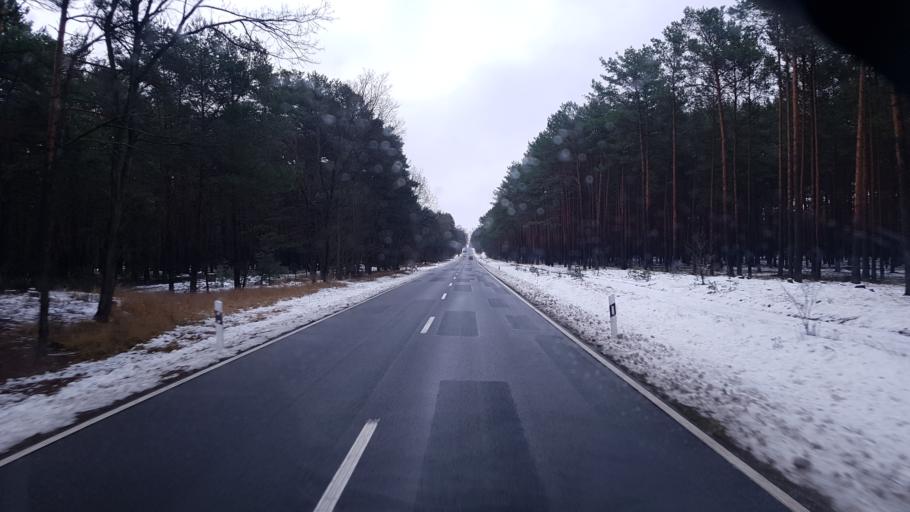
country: DE
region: Brandenburg
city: Jamlitz
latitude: 51.9834
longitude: 14.4325
